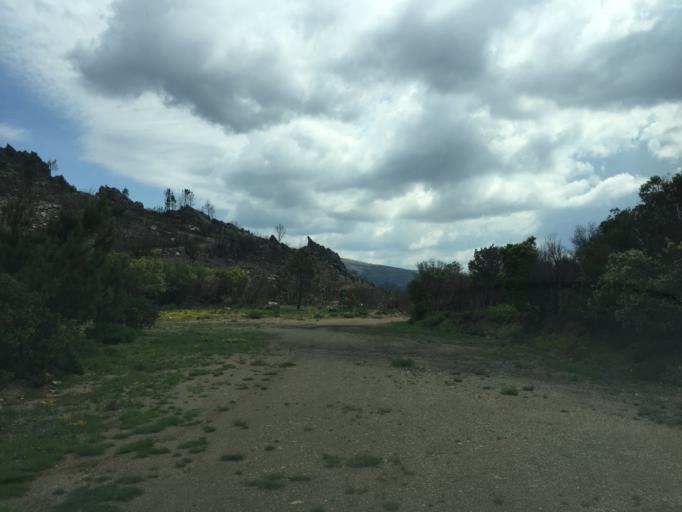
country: PT
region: Coimbra
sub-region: Pampilhosa da Serra
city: Pampilhosa da Serra
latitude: 40.1590
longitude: -7.9301
